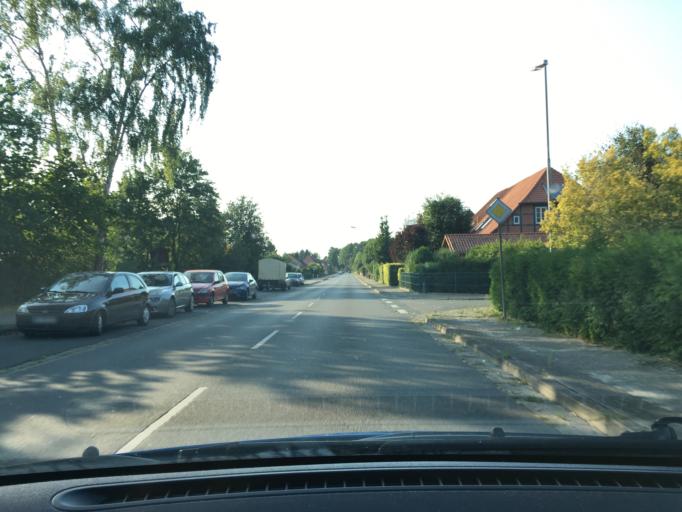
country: DE
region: Lower Saxony
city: Bienenbuttel
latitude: 53.1364
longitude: 10.5057
